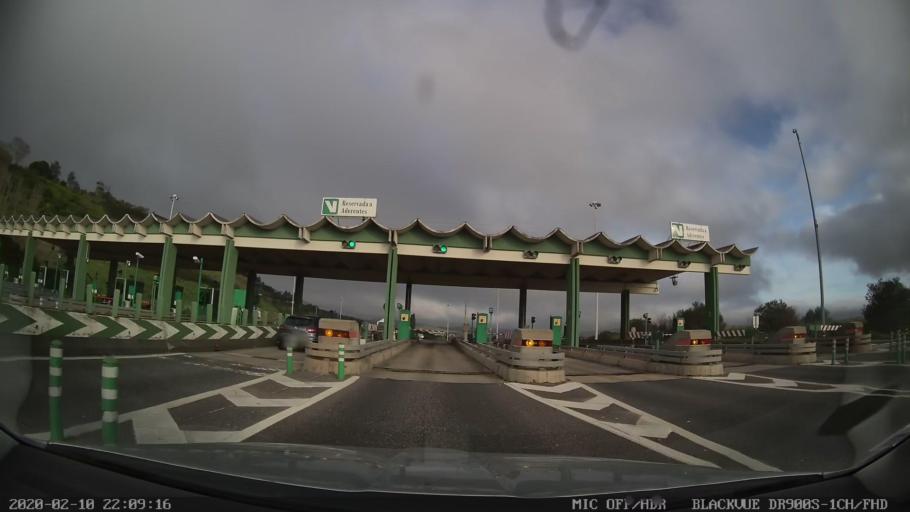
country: PT
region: Lisbon
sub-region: Odivelas
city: Ramada
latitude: 38.8197
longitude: -9.1870
